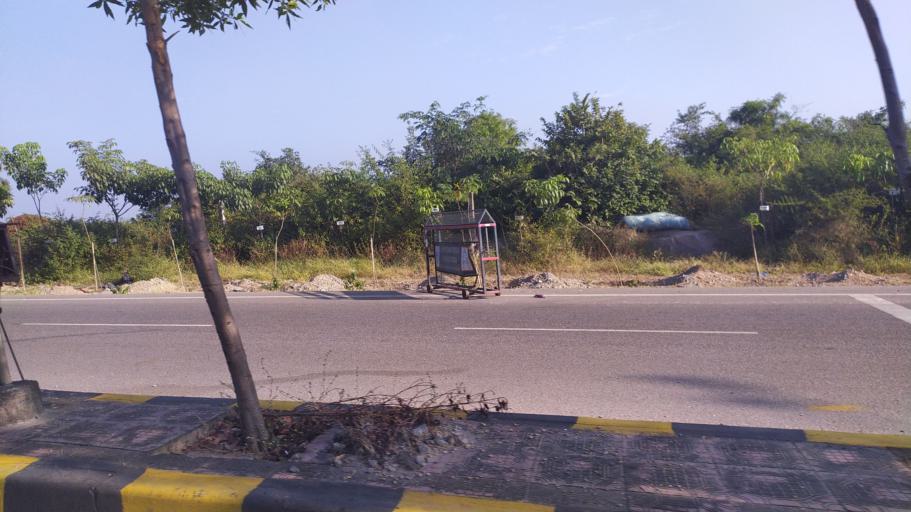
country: IN
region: Telangana
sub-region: Hyderabad
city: Hyderabad
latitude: 17.3215
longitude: 78.3853
